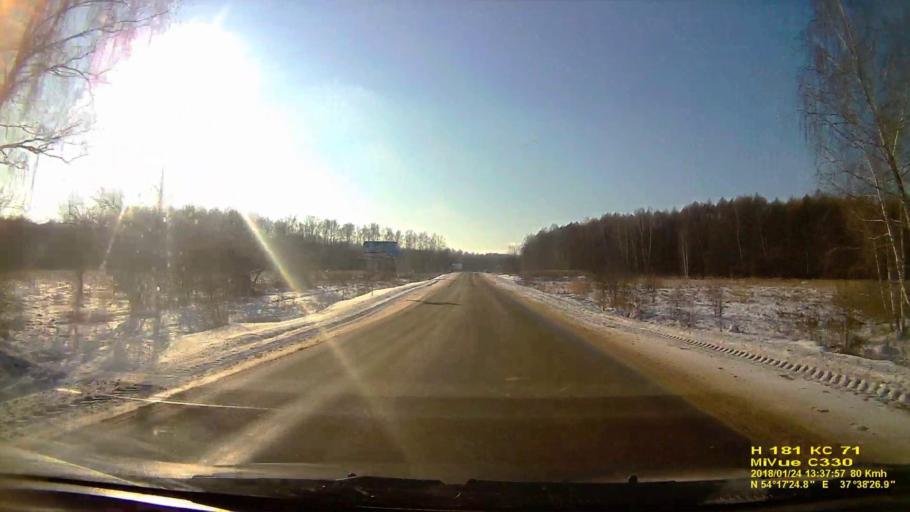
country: RU
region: Tula
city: Gorelki
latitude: 54.2901
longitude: 37.6405
